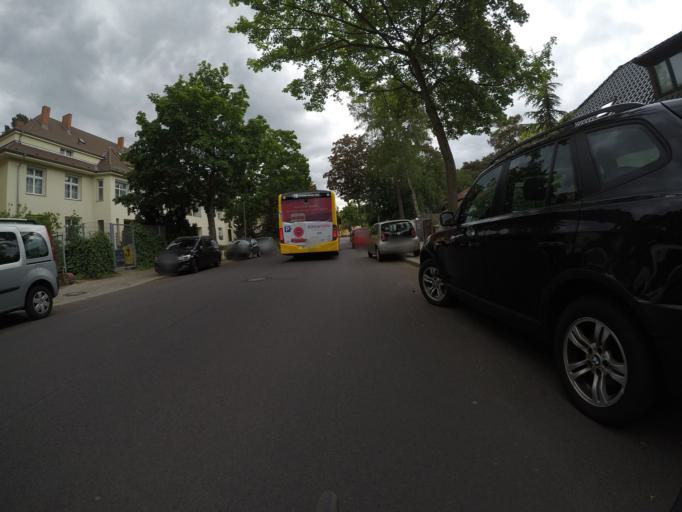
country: DE
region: Berlin
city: Schmargendorf
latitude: 52.4839
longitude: 13.2851
